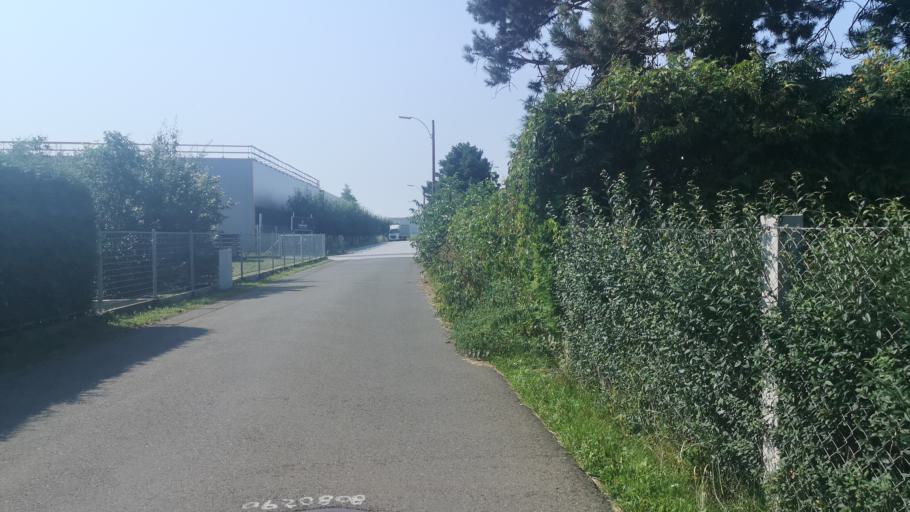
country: AT
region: Styria
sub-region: Politischer Bezirk Graz-Umgebung
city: Seiersberg
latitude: 47.0230
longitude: 15.4083
